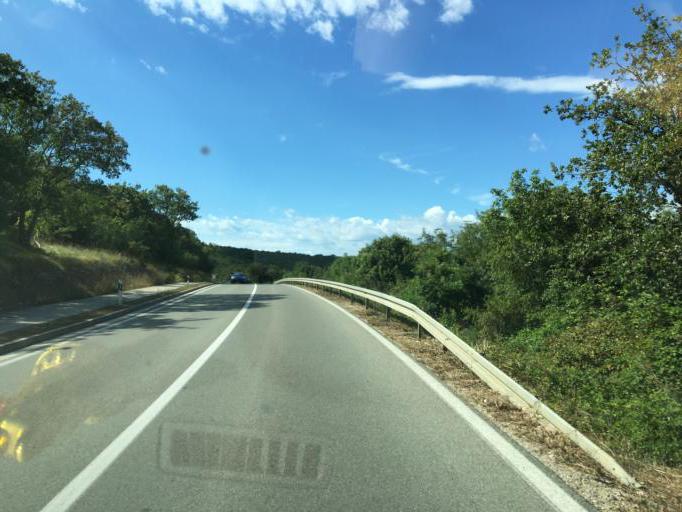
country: HR
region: Primorsko-Goranska
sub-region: Grad Krk
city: Krk
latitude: 45.0742
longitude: 14.5497
